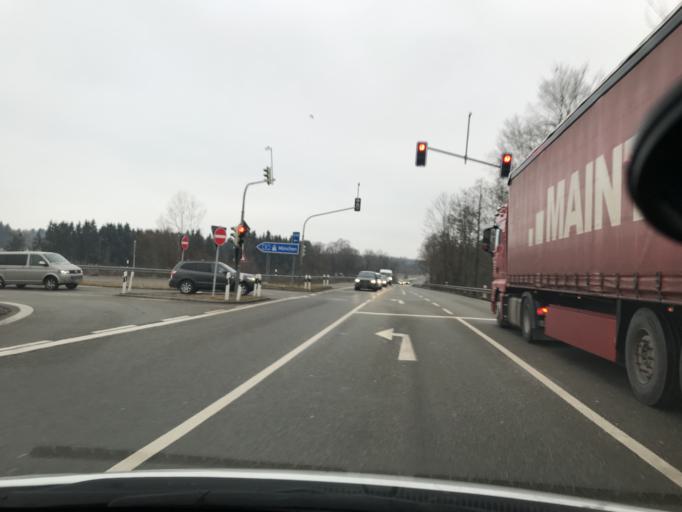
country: DE
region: Bavaria
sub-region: Upper Bavaria
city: Bad Aibling
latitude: 47.8216
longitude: 12.0140
